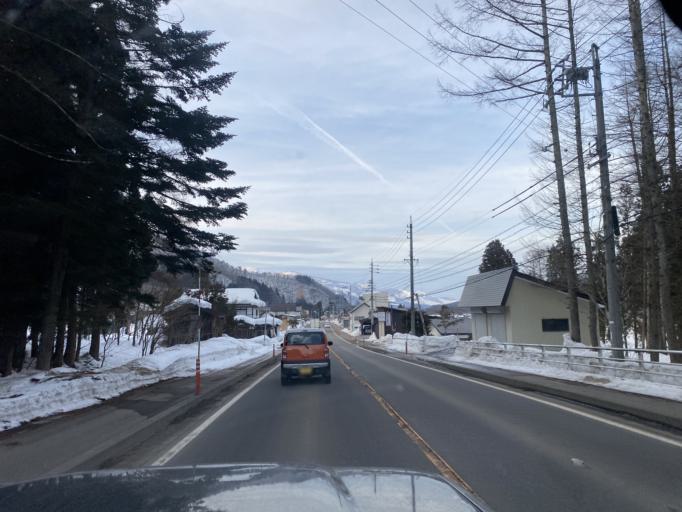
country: JP
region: Nagano
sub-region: Kitaazumi Gun
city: Hakuba
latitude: 36.6383
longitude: 137.8448
